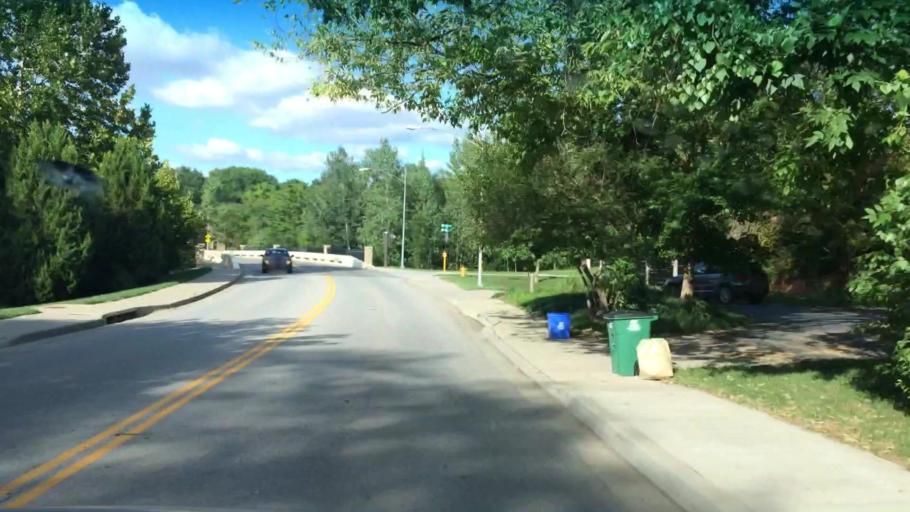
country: US
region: Kansas
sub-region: Johnson County
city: Fairway
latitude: 39.0279
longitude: -94.6266
